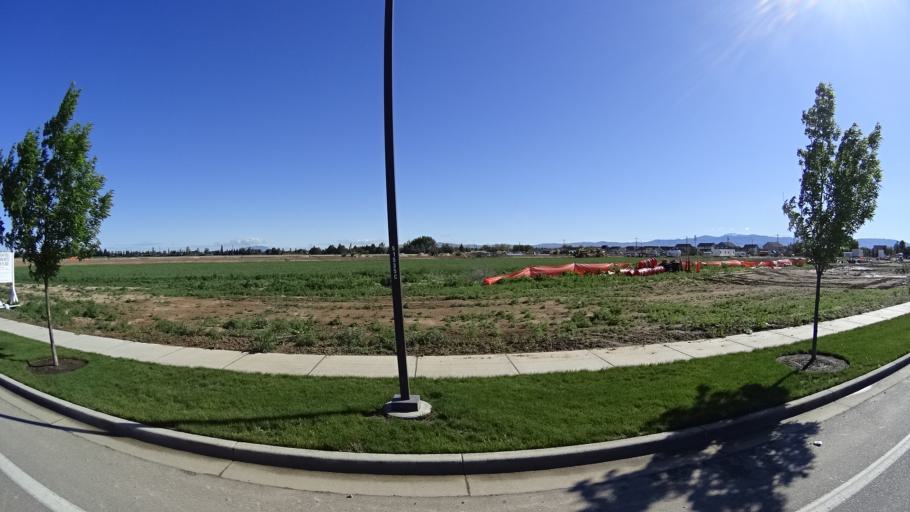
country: US
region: Idaho
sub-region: Ada County
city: Meridian
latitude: 43.6590
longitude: -116.4366
